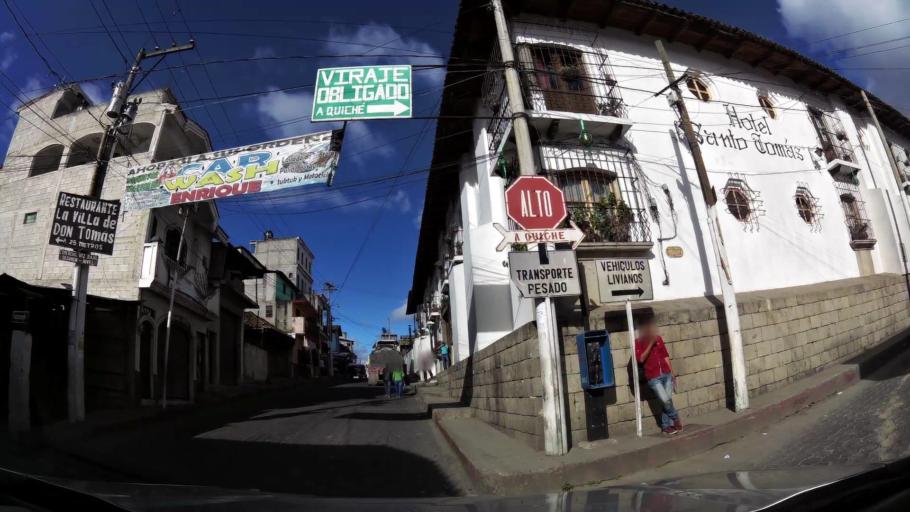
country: GT
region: Quiche
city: Chichicastenango
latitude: 14.9428
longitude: -91.1099
